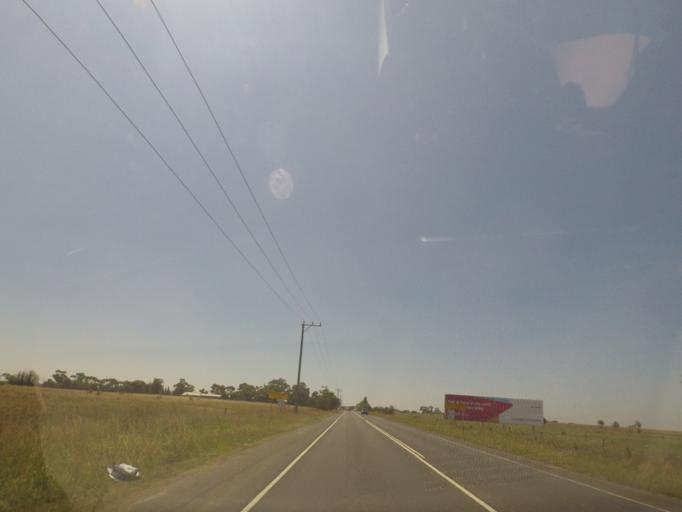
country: AU
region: Victoria
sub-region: Hume
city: Craigieburn
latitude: -37.6033
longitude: 144.9784
